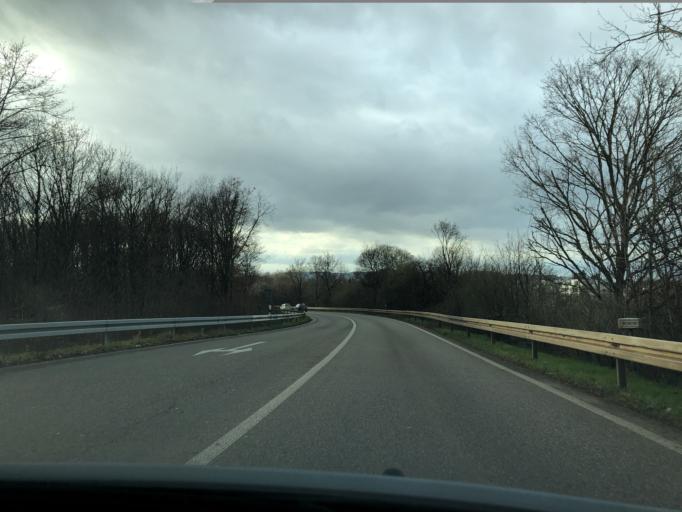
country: DE
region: Baden-Wuerttemberg
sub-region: Freiburg Region
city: Freiburg
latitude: 48.0018
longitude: 7.8149
